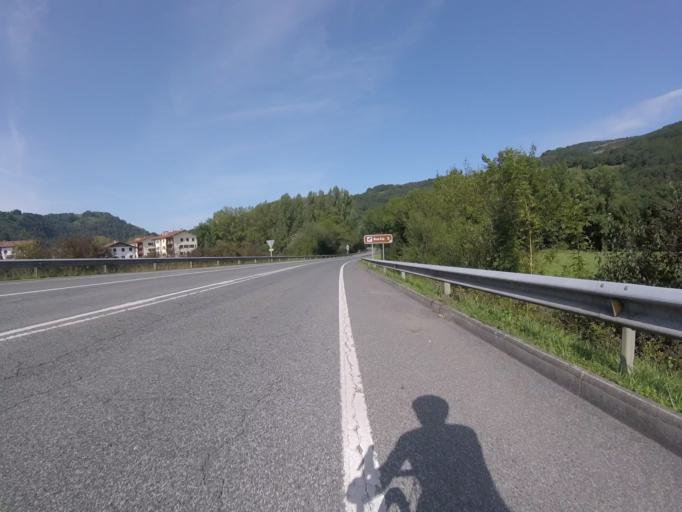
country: ES
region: Navarre
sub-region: Provincia de Navarra
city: Doneztebe
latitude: 43.1415
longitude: -1.5640
